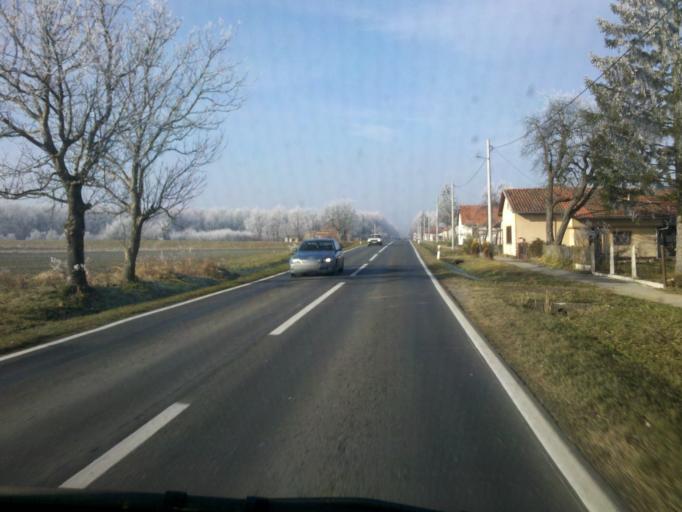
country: HR
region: Koprivnicko-Krizevacka
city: Kalinovac
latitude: 45.9897
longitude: 17.1330
